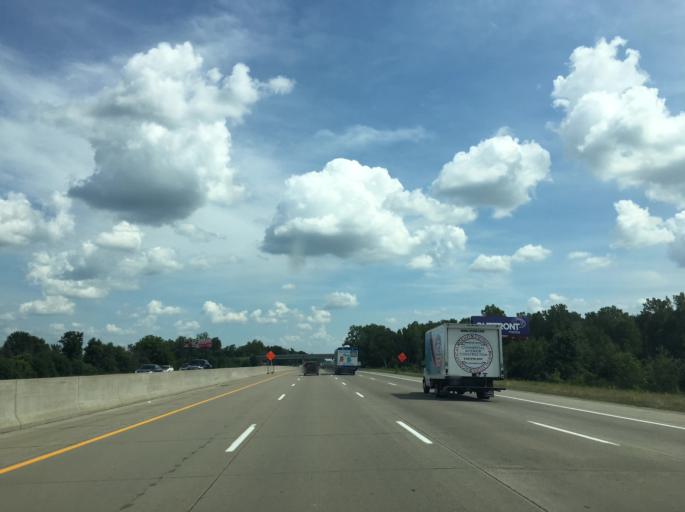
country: US
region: Michigan
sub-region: Saginaw County
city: Birch Run
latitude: 43.2963
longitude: -83.8230
